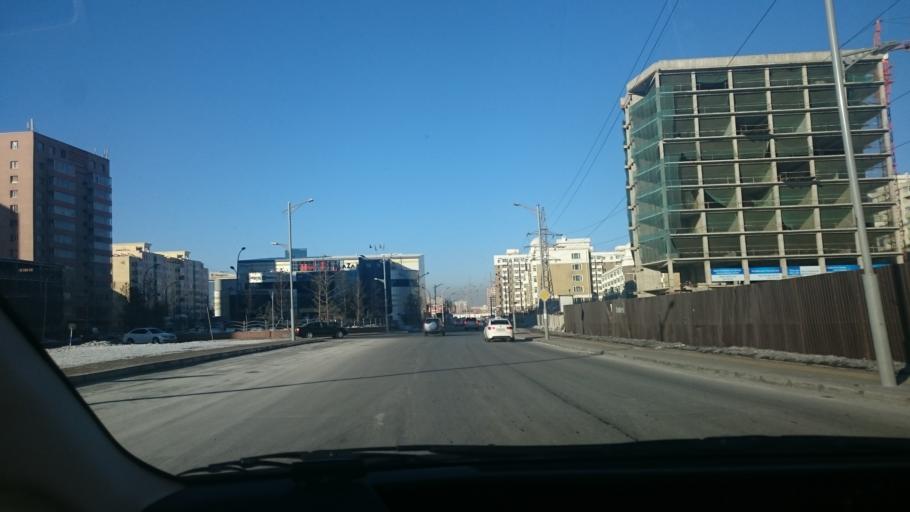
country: MN
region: Ulaanbaatar
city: Ulaanbaatar
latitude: 47.9028
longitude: 106.9286
